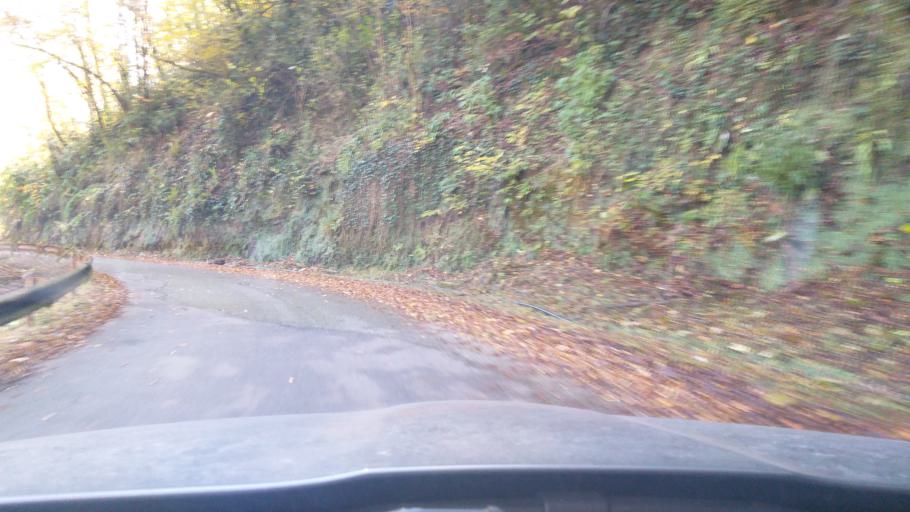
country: GE
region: Abkhazia
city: Bich'vinta
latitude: 43.1871
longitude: 40.4526
